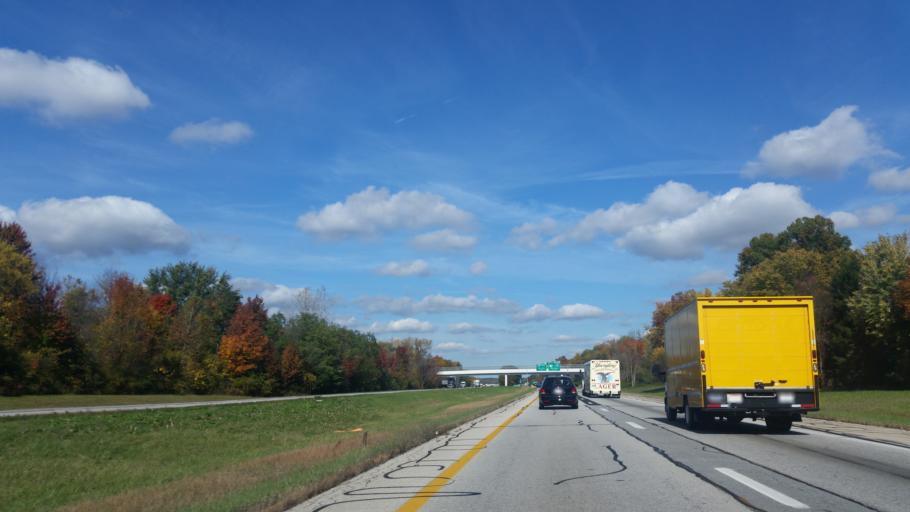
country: US
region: Ohio
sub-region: Summit County
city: Richfield
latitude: 41.2087
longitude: -81.6255
